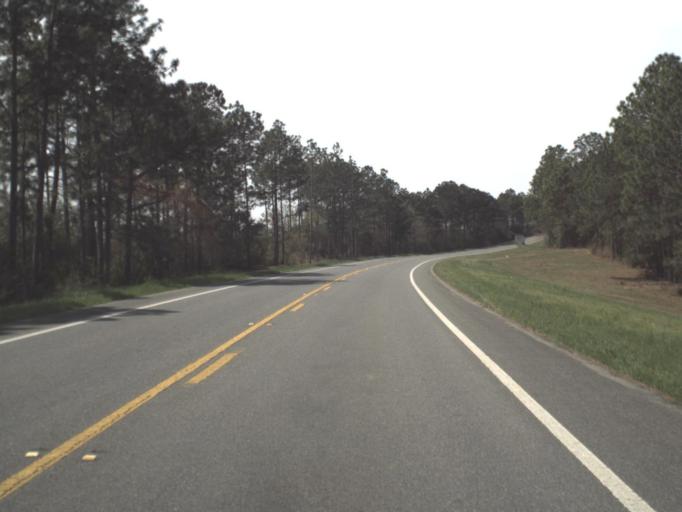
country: US
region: Florida
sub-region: Walton County
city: DeFuniak Springs
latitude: 30.7226
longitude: -85.9797
